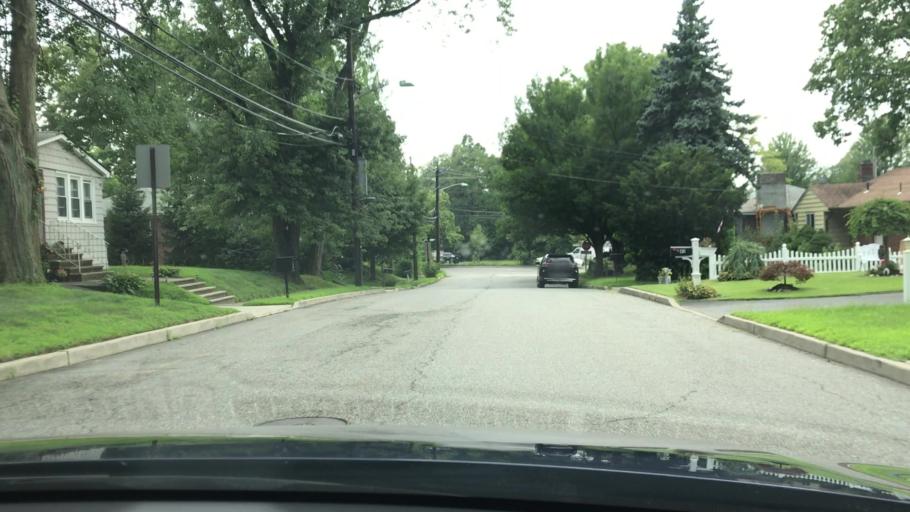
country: US
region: New Jersey
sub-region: Bergen County
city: Rochelle Park
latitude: 40.9217
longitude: -74.0852
